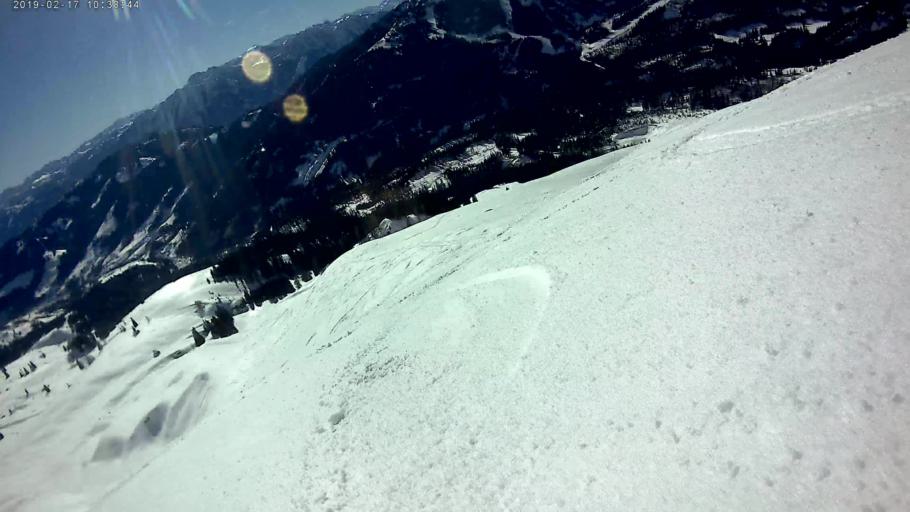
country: AT
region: Salzburg
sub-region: Politischer Bezirk Sankt Johann im Pongau
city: Muhlbach am Hochkonig
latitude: 47.4069
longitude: 13.0811
